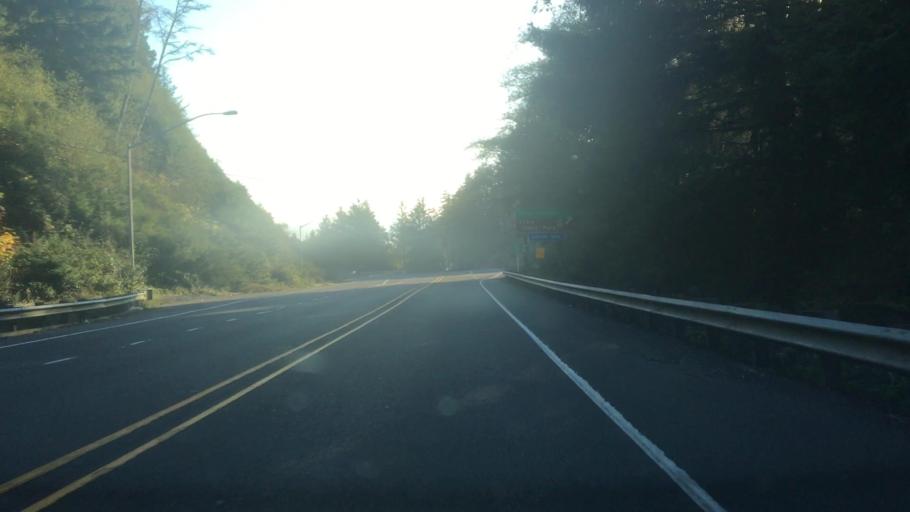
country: US
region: Oregon
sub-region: Clatsop County
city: Cannon Beach
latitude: 45.9082
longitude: -123.9520
